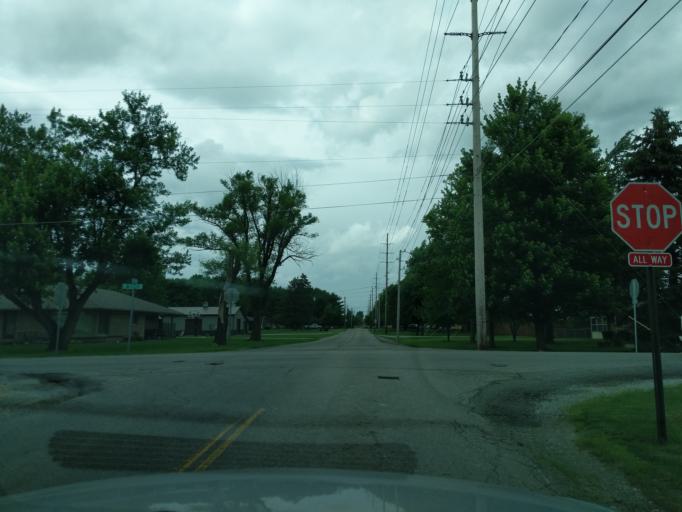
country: US
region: Indiana
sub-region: Madison County
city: Edgewood
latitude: 40.0611
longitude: -85.7302
